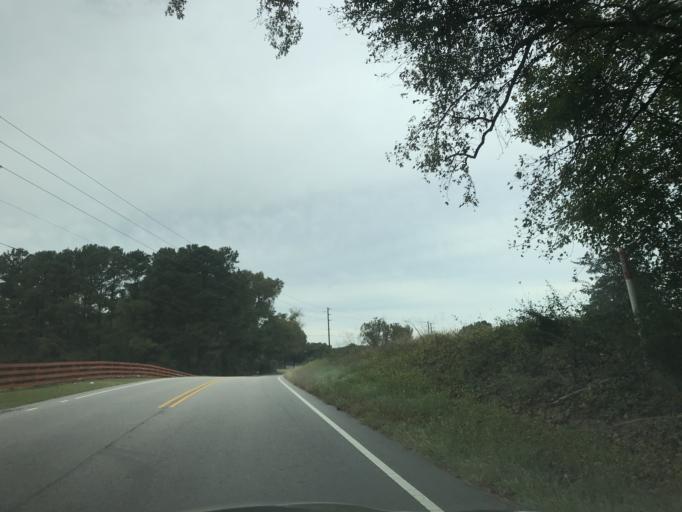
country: US
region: North Carolina
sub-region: Wake County
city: Knightdale
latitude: 35.8601
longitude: -78.5132
